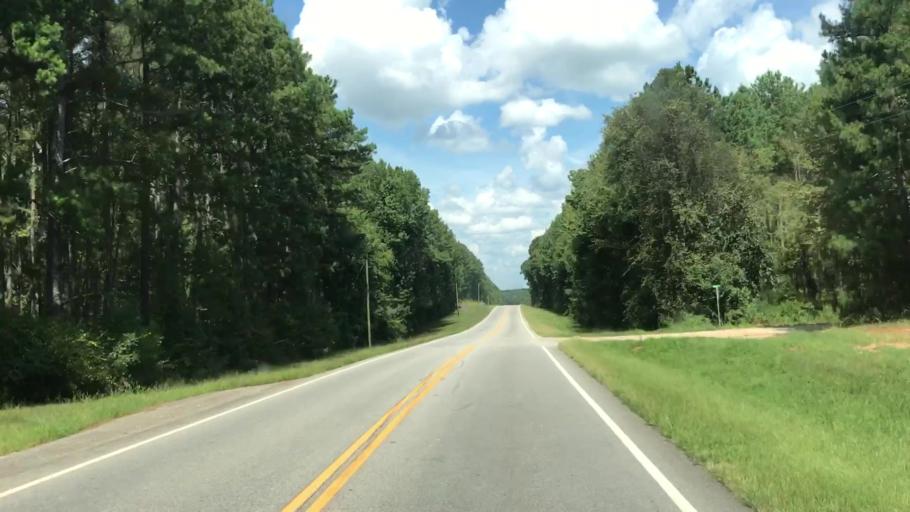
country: US
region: Georgia
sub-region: Greene County
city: Greensboro
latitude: 33.6817
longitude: -83.2721
